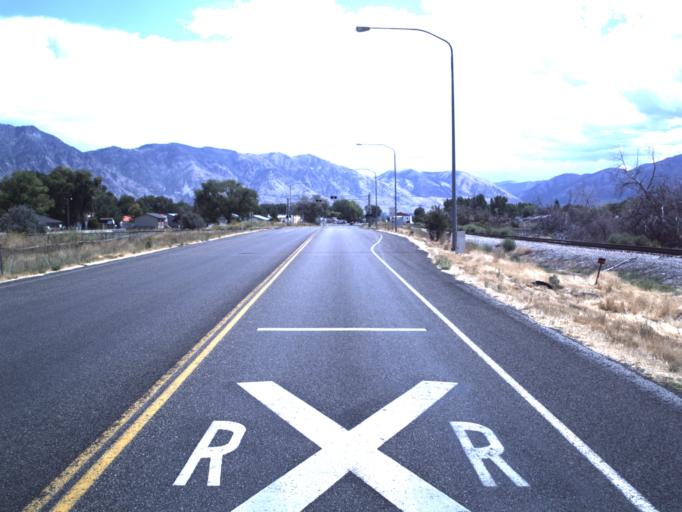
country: US
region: Utah
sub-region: Box Elder County
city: Honeyville
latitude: 41.5527
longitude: -112.1177
